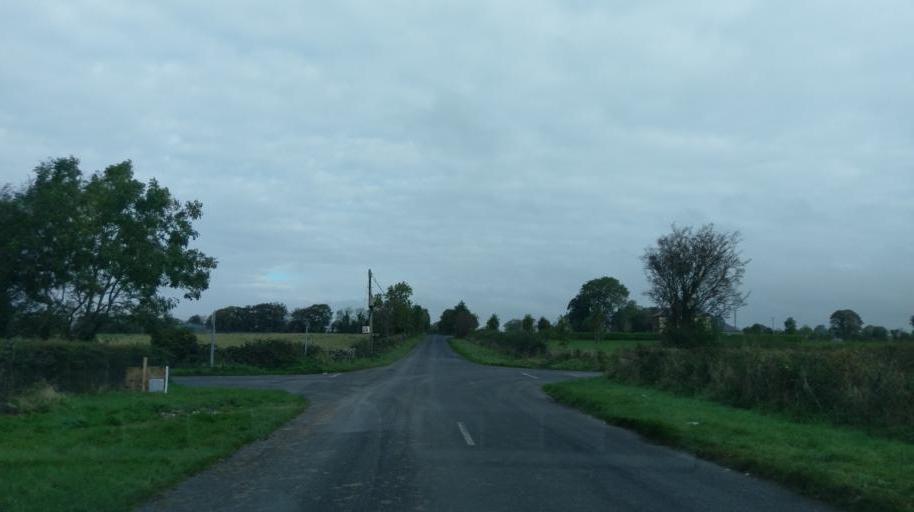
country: IE
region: Connaught
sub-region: County Galway
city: Athenry
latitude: 53.4307
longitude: -8.6401
